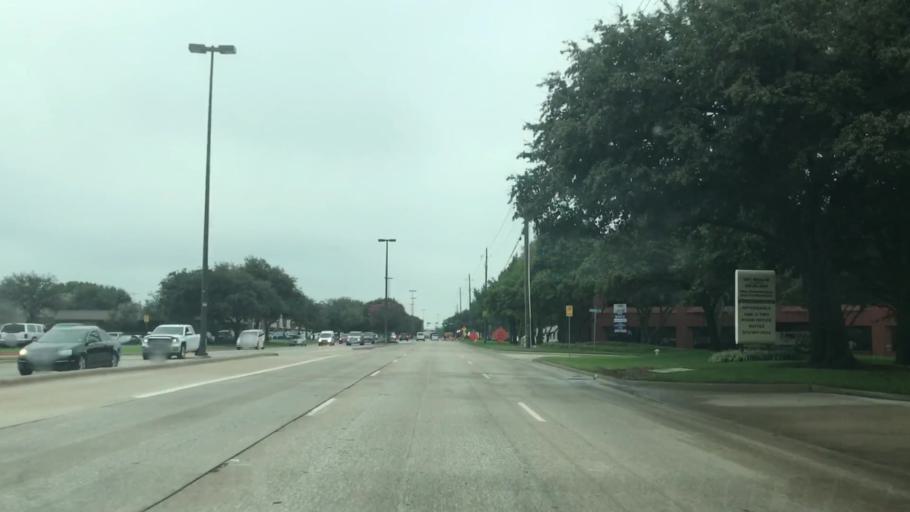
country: US
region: Texas
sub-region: Dallas County
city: Addison
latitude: 32.9677
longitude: -96.8410
